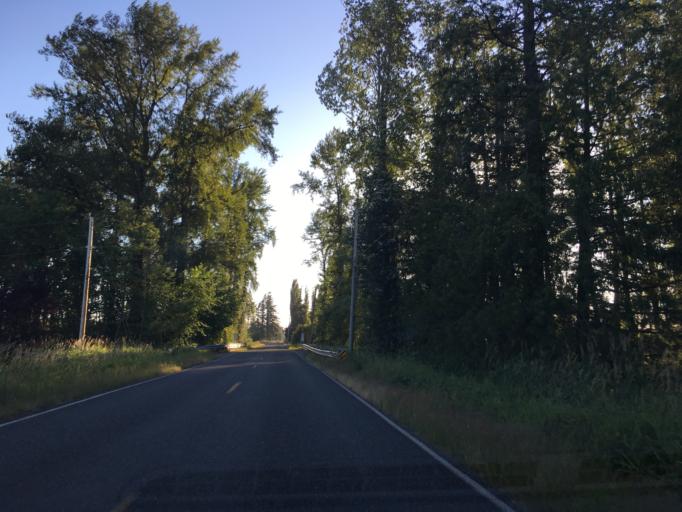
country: US
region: Washington
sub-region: Whatcom County
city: Sudden Valley
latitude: 48.8181
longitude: -122.3388
